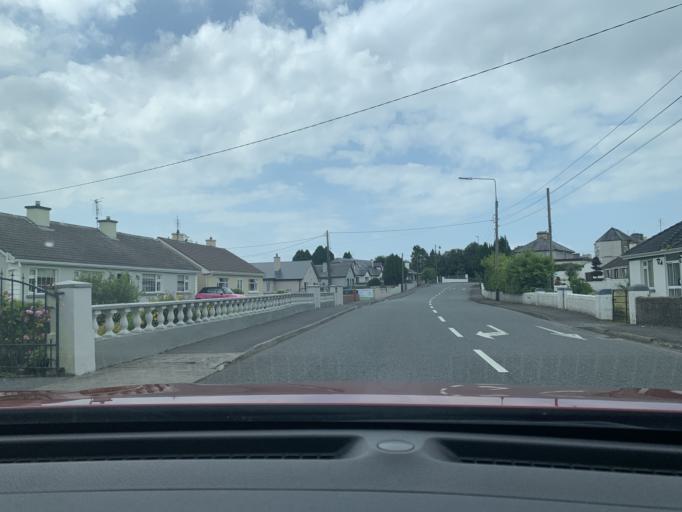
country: IE
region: Connaught
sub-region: Maigh Eo
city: Kiltamagh
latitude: 53.8489
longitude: -8.9941
